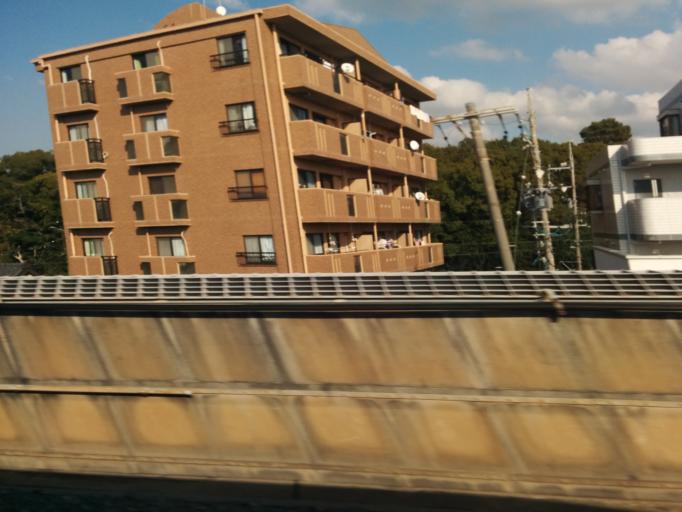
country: JP
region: Aichi
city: Toyohashi
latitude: 34.7492
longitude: 137.3900
